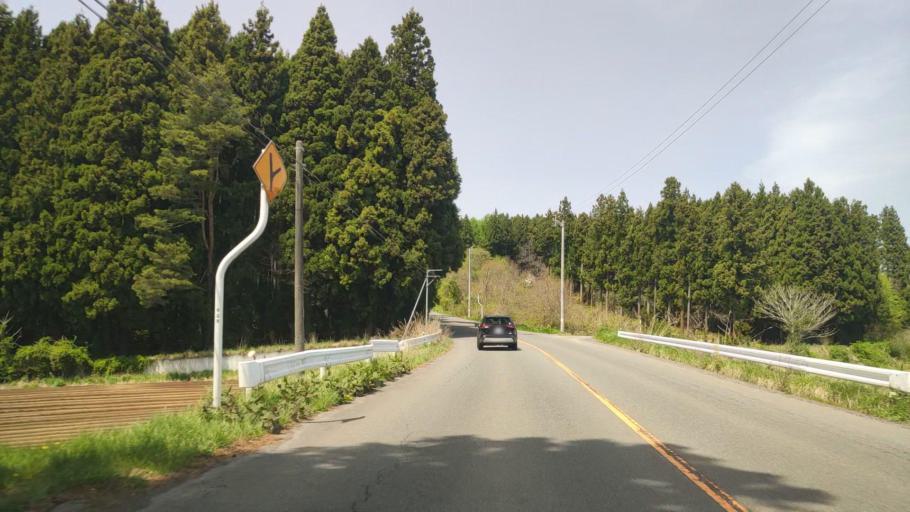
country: JP
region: Aomori
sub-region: Misawa Shi
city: Inuotose
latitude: 40.5683
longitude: 141.3780
